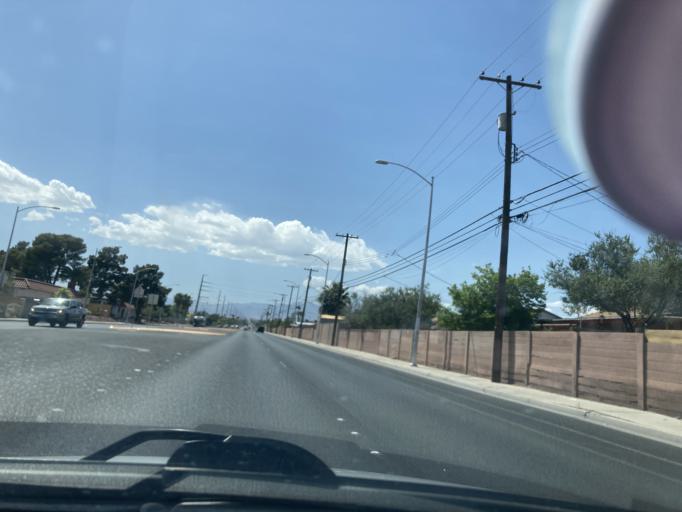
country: US
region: Nevada
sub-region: Clark County
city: North Las Vegas
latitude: 36.1810
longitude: -115.0946
